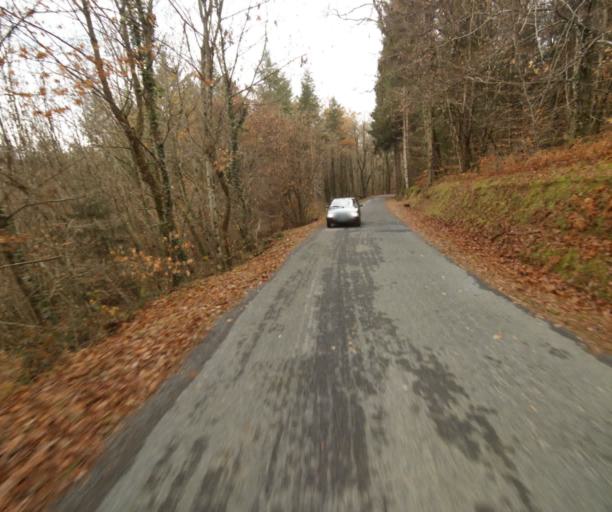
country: FR
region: Limousin
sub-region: Departement de la Correze
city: Sainte-Fortunade
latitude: 45.2225
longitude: 1.7493
